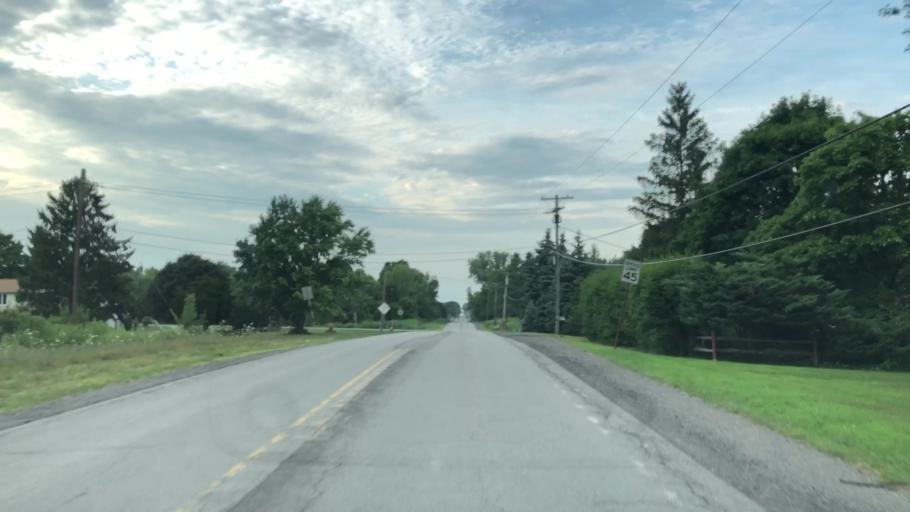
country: US
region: New York
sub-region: Erie County
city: Billington Heights
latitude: 42.7909
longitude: -78.6059
